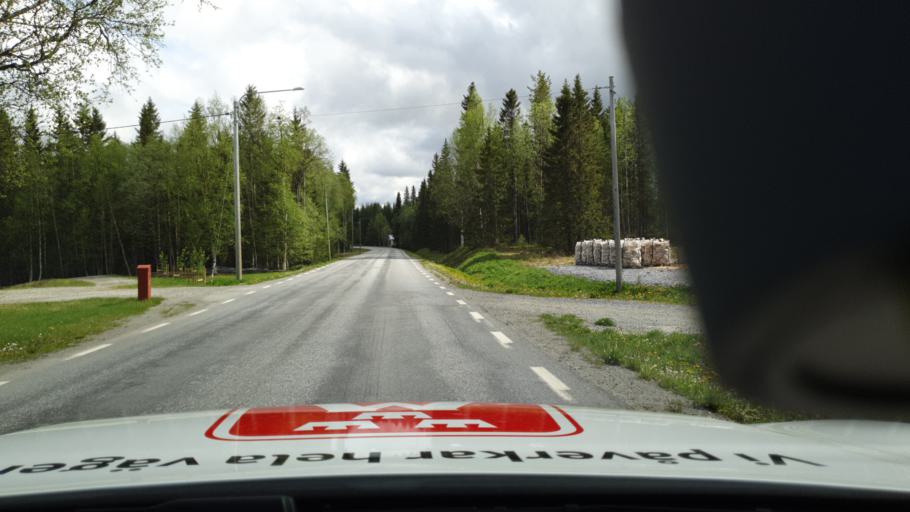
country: SE
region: Vaesterbotten
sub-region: Vilhelmina Kommun
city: Sjoberg
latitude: 64.6536
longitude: 16.3223
